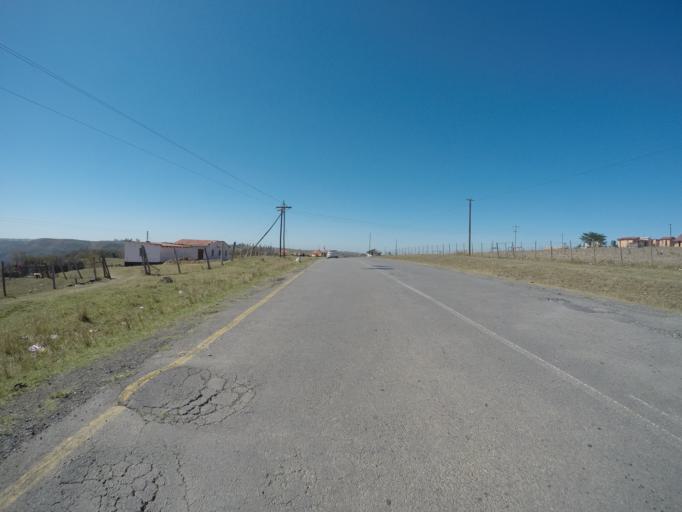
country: ZA
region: Eastern Cape
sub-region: OR Tambo District Municipality
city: Mthatha
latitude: -31.9079
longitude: 28.9496
